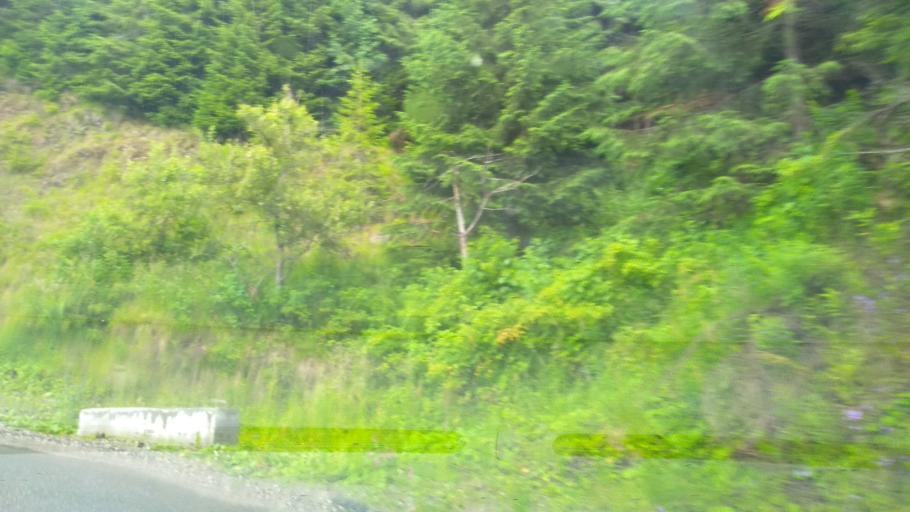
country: RO
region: Hunedoara
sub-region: Oras Petrila
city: Petrila
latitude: 45.4069
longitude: 23.5778
